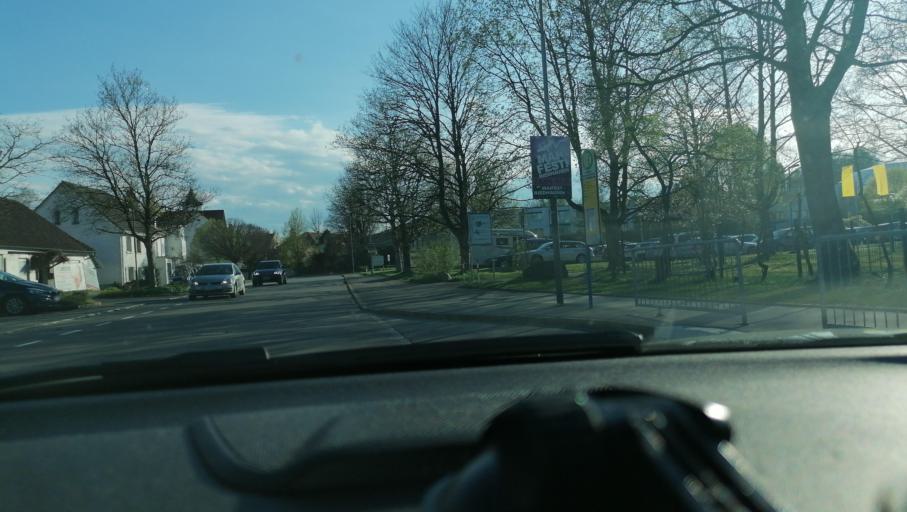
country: DE
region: Baden-Wuerttemberg
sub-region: Tuebingen Region
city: Aulendorf
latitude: 47.9570
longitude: 9.6407
